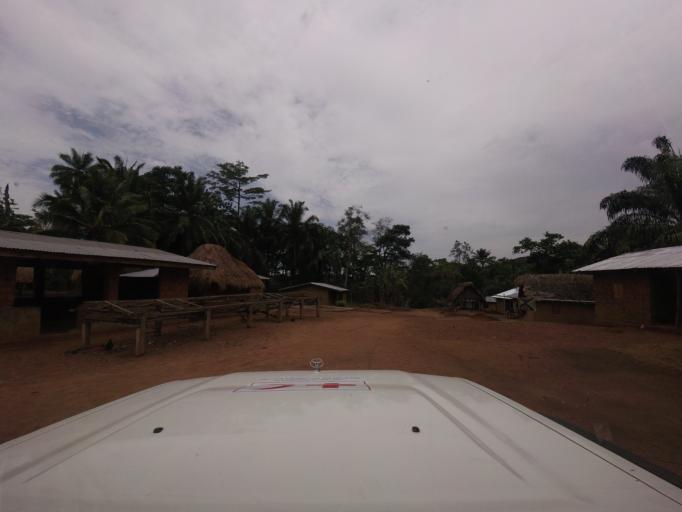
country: SL
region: Eastern Province
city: Buedu
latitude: 8.2299
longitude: -10.2933
